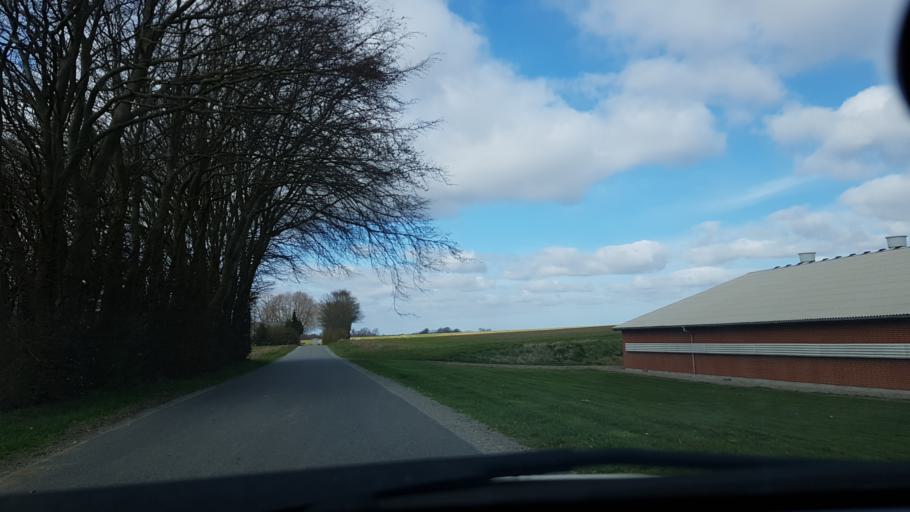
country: DK
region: South Denmark
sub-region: Vejen Kommune
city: Rodding
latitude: 55.4053
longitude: 9.0152
